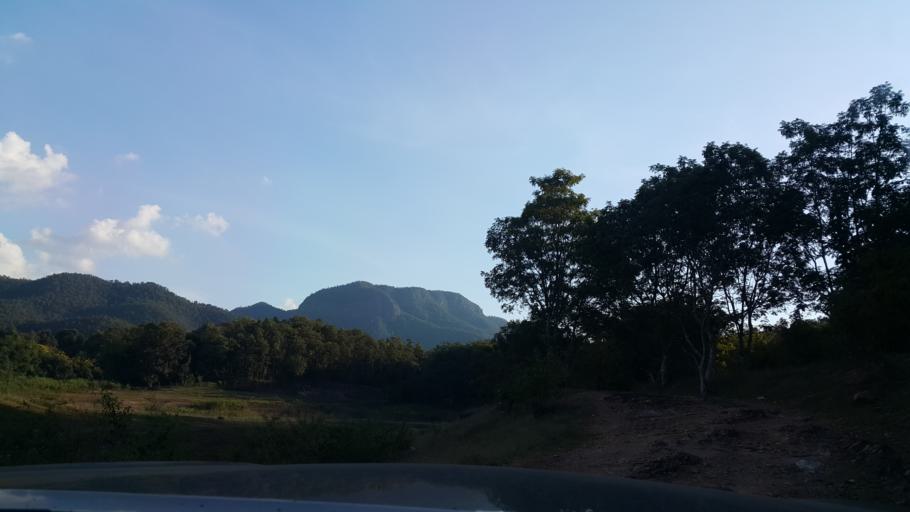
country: TH
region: Chiang Mai
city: Mae On
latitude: 18.6992
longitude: 99.2007
